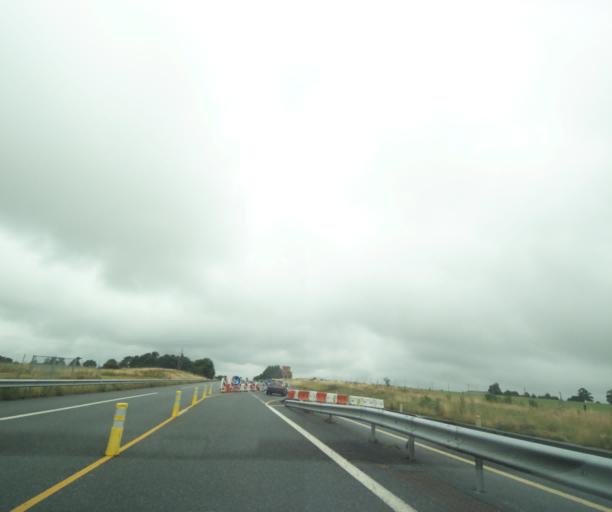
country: FR
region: Midi-Pyrenees
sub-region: Departement de l'Aveyron
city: Luc-la-Primaube
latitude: 44.2953
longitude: 2.5215
